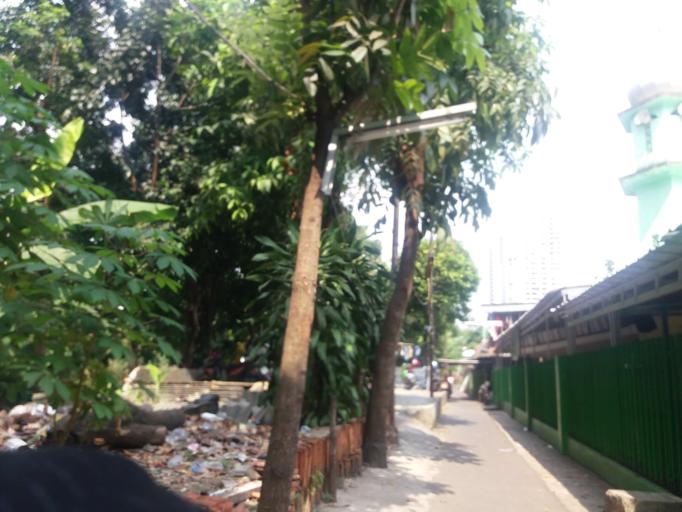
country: ID
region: Jakarta Raya
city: Jakarta
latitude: -6.2229
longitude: 106.8173
